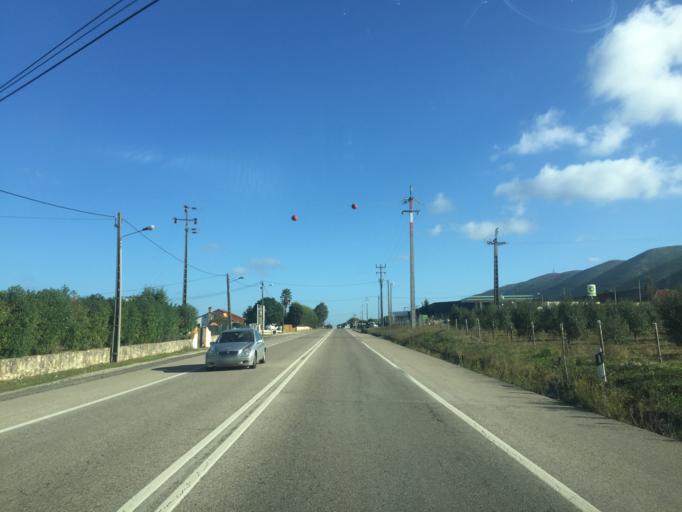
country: PT
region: Leiria
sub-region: Alcobaca
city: Aljubarrota
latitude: 39.5238
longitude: -8.9119
